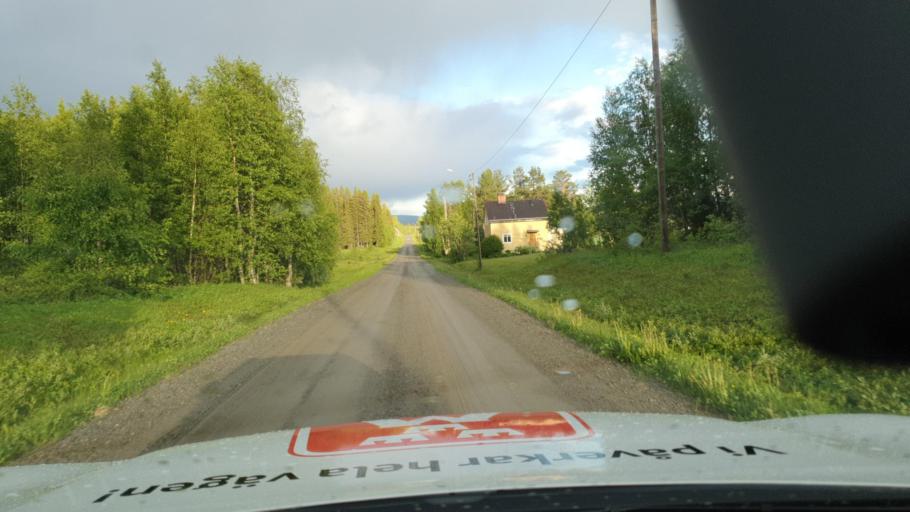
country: SE
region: Vaesterbotten
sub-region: Storumans Kommun
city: Storuman
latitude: 64.7641
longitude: 17.0598
